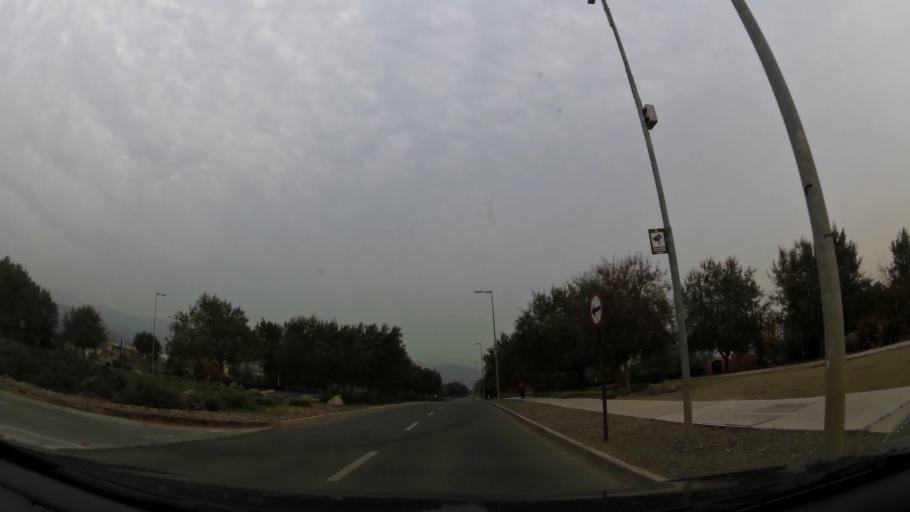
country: CL
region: Santiago Metropolitan
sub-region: Provincia de Chacabuco
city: Chicureo Abajo
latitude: -33.2586
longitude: -70.6272
